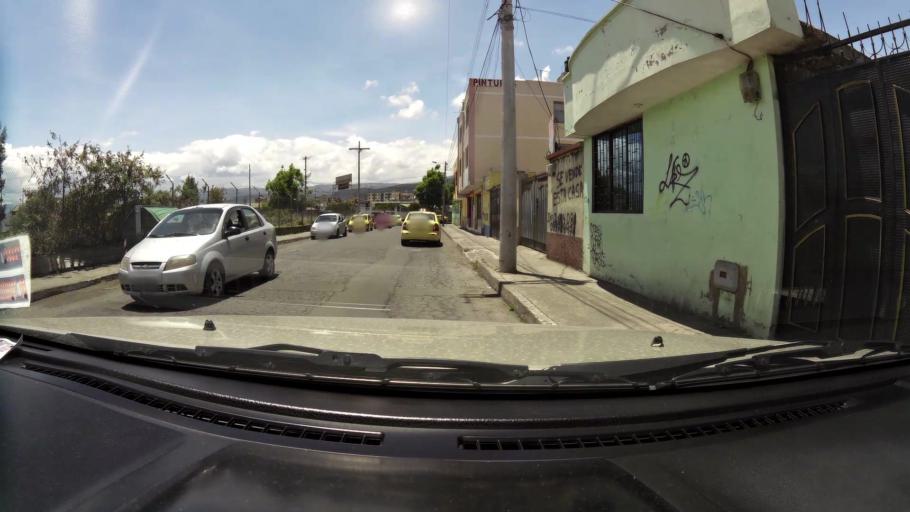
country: EC
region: Chimborazo
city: Riobamba
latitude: -1.6781
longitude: -78.6385
